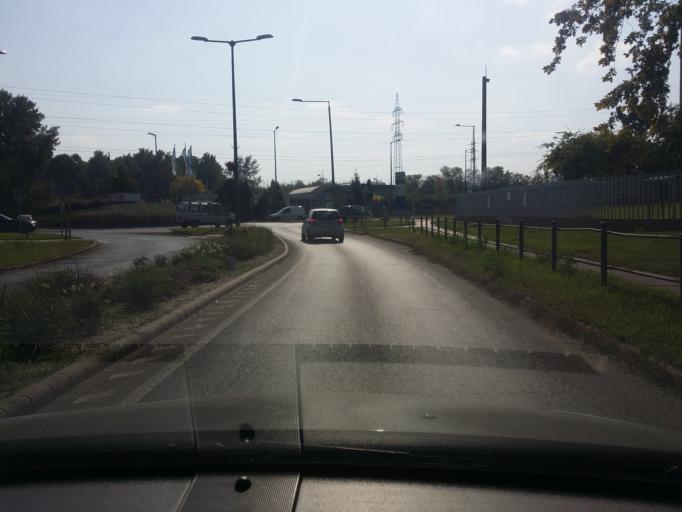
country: HU
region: Fejer
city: dunaujvaros
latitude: 46.9590
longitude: 18.9202
